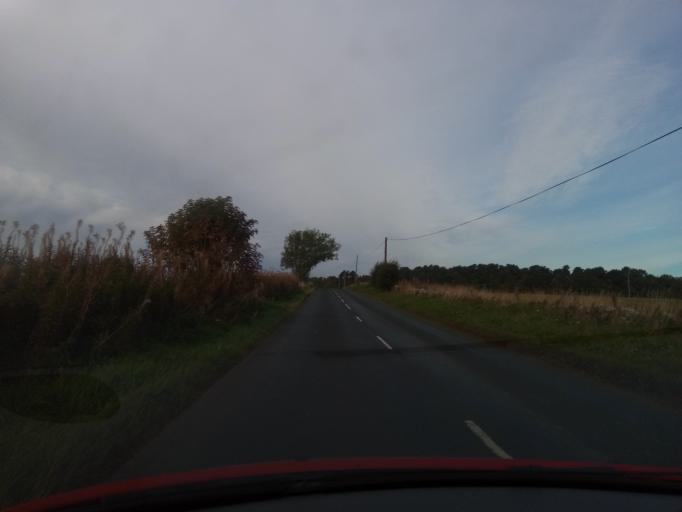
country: GB
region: Scotland
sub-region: The Scottish Borders
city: Kelso
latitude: 55.5639
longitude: -2.3436
